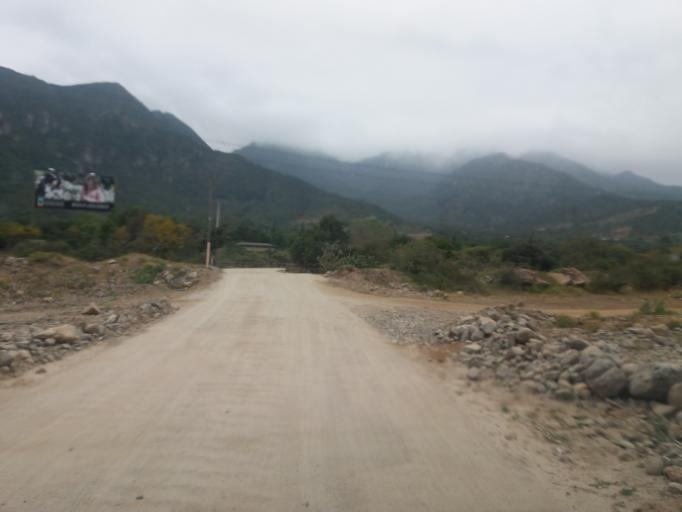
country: CL
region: Valparaiso
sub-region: Provincia de Marga Marga
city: Limache
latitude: -33.0281
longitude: -71.1419
